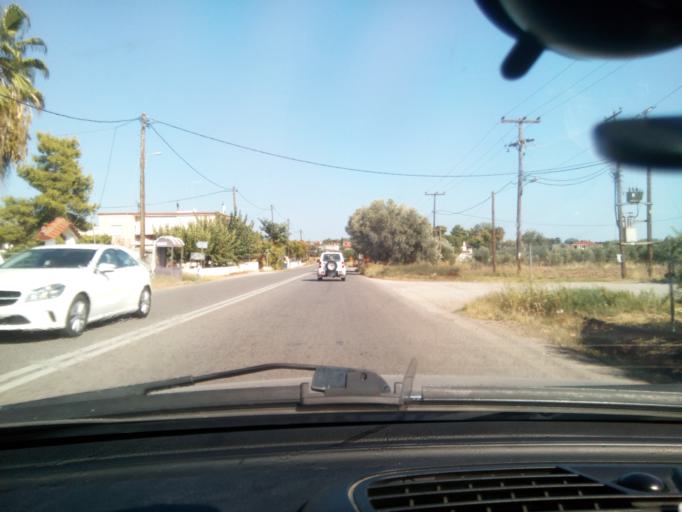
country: GR
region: Central Greece
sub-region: Nomos Evvoias
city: Malakonta
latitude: 38.4051
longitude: 23.7454
